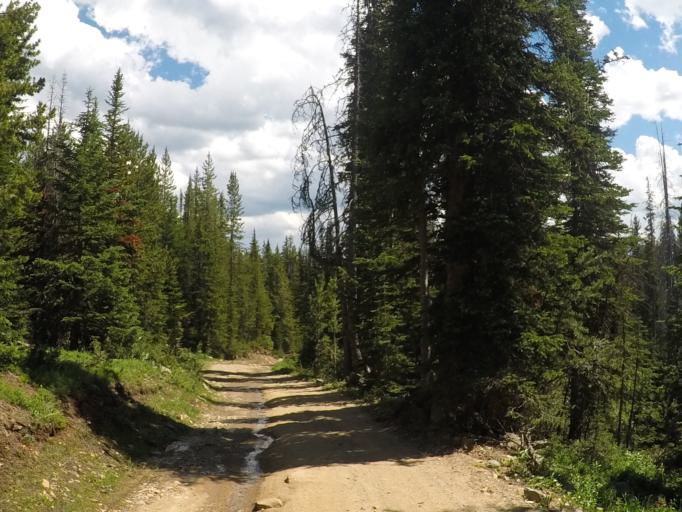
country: US
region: Montana
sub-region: Stillwater County
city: Absarokee
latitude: 45.0403
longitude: -109.9081
